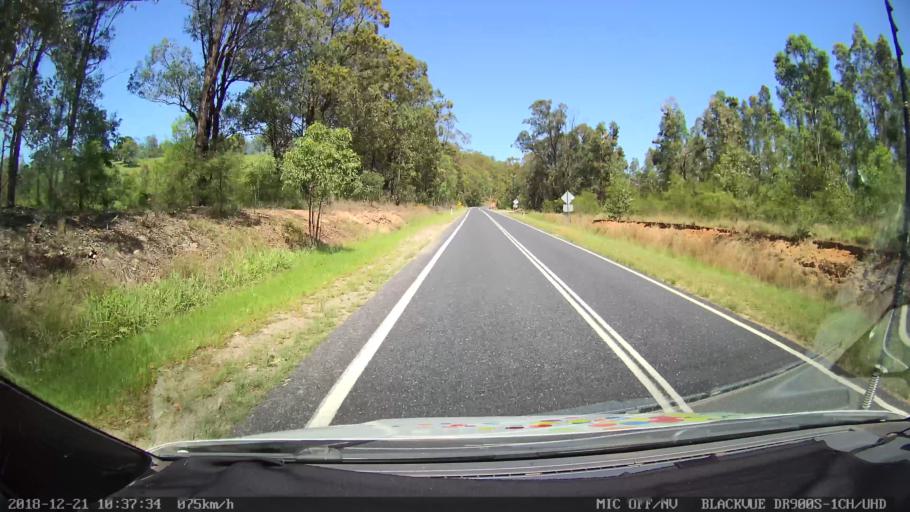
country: AU
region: New South Wales
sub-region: Clarence Valley
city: South Grafton
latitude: -29.6226
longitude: 152.6170
